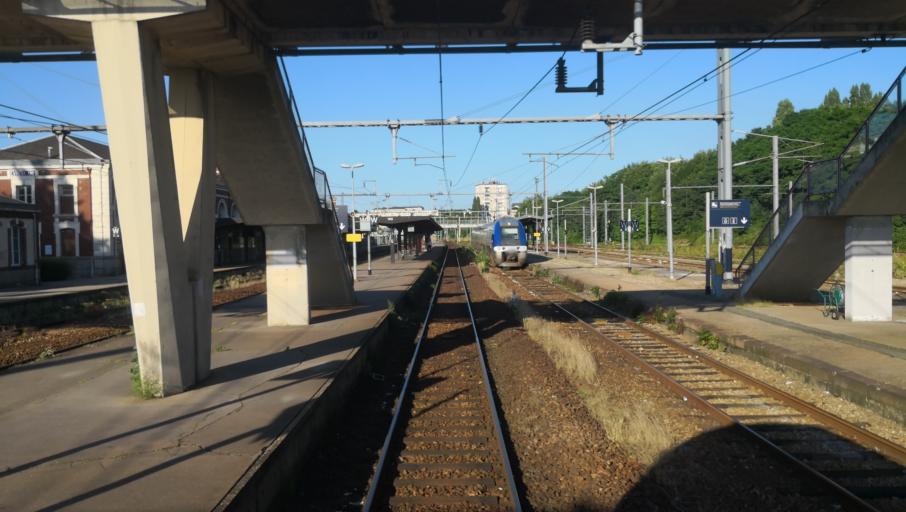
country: FR
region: Haute-Normandie
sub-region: Departement de l'Eure
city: Evreux
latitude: 49.0185
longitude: 1.1502
